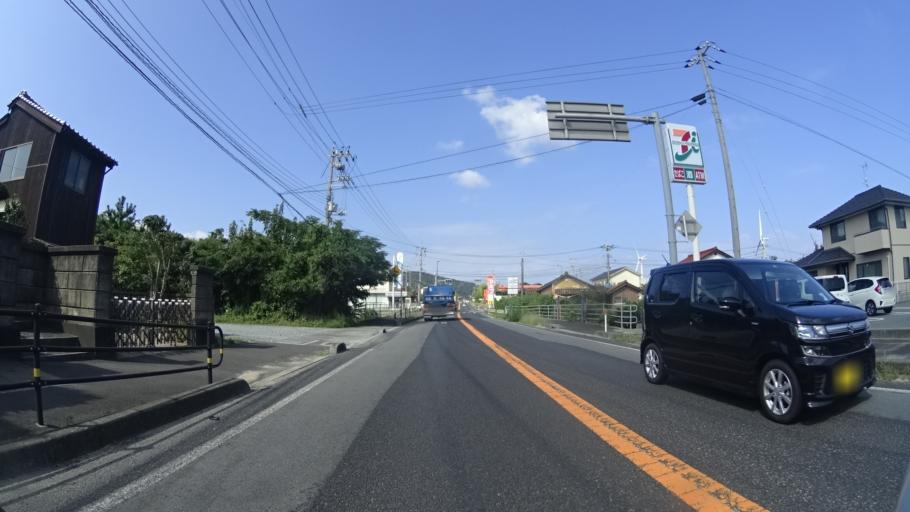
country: JP
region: Shimane
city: Gotsucho
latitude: 35.0365
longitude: 132.2782
